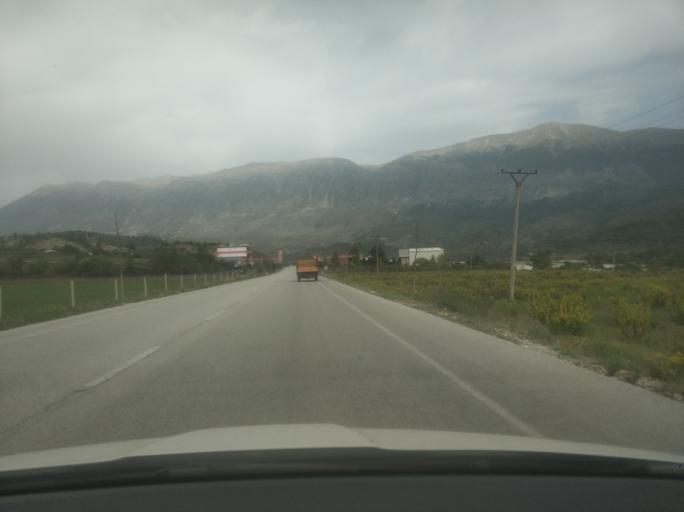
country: AL
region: Gjirokaster
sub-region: Rrethi i Gjirokastres
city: Picar
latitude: 40.1852
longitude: 20.0774
